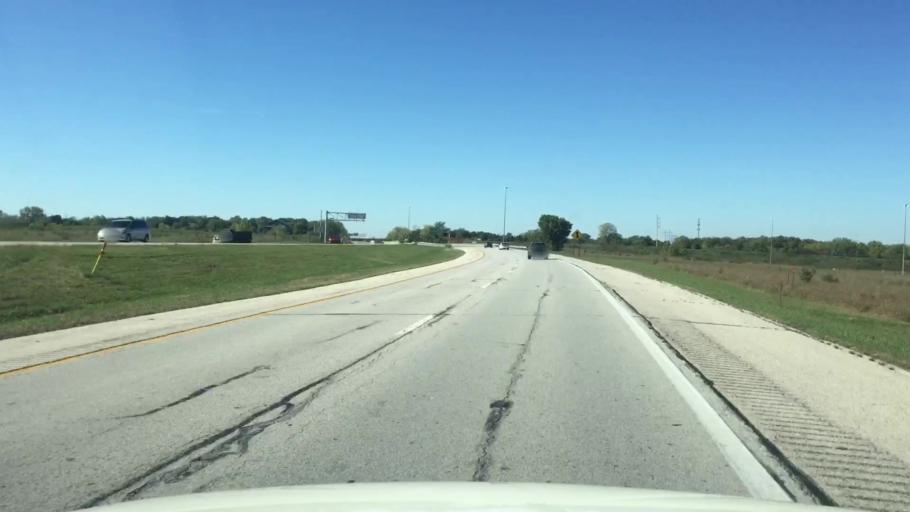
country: US
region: Kansas
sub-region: Wyandotte County
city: Edwardsville
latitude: 39.0105
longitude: -94.7812
